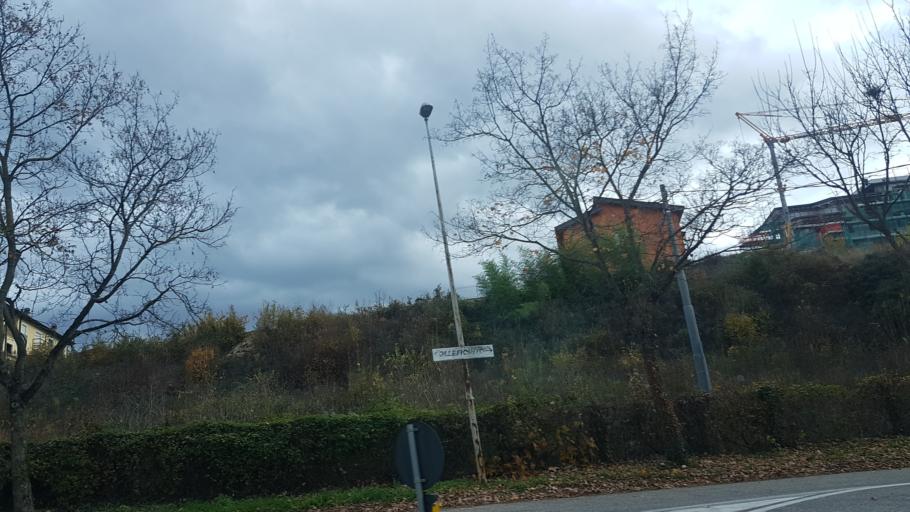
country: IT
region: Abruzzo
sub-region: Provincia dell' Aquila
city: L'Aquila
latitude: 42.3448
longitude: 13.4095
